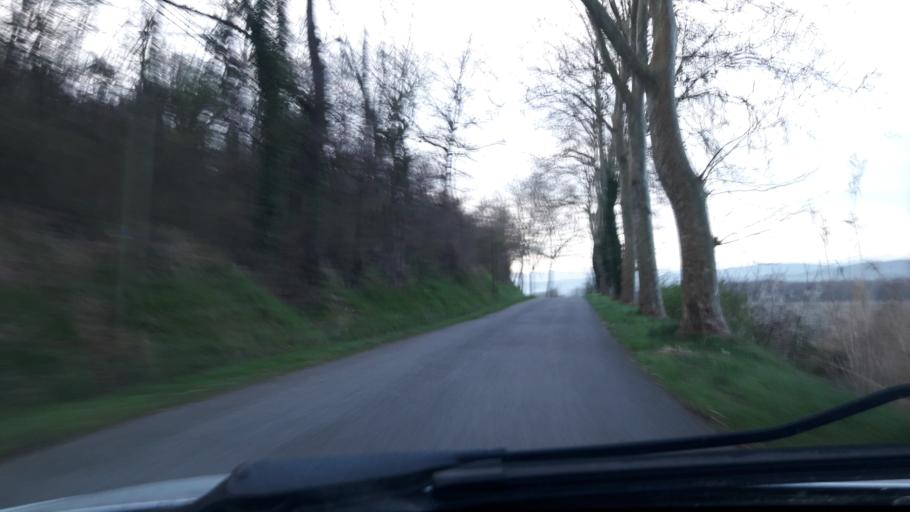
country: FR
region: Midi-Pyrenees
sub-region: Departement de la Haute-Garonne
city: Montesquieu-Volvestre
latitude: 43.1963
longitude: 1.2481
